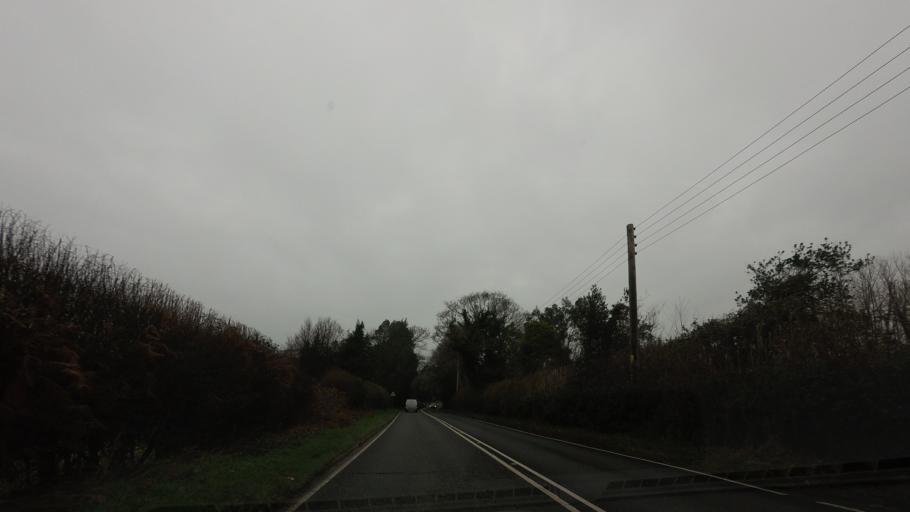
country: GB
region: England
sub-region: East Sussex
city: Battle
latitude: 50.9489
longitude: 0.5069
